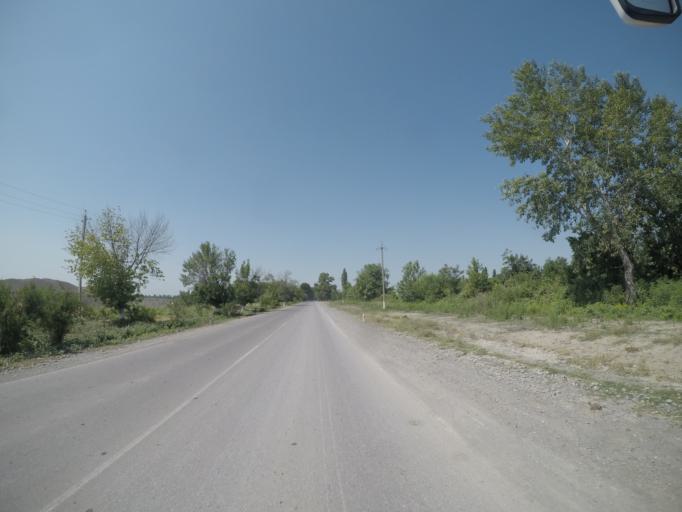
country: AZ
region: Agdas
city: Agdas
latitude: 40.6806
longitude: 47.5290
